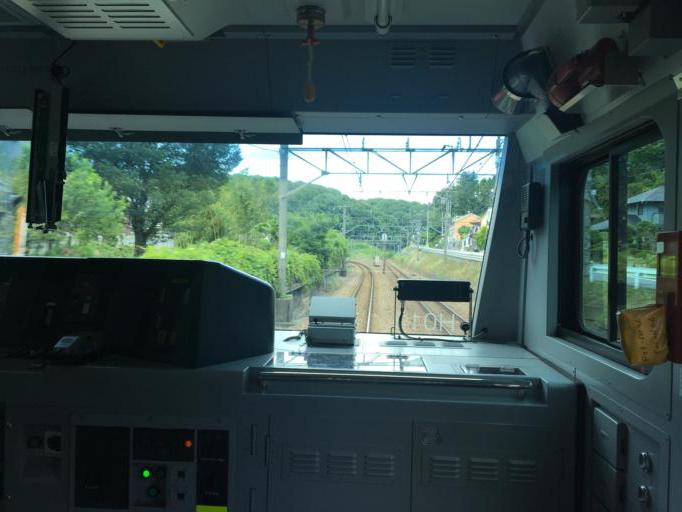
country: JP
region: Tokyo
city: Hachioji
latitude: 35.6089
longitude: 139.3315
